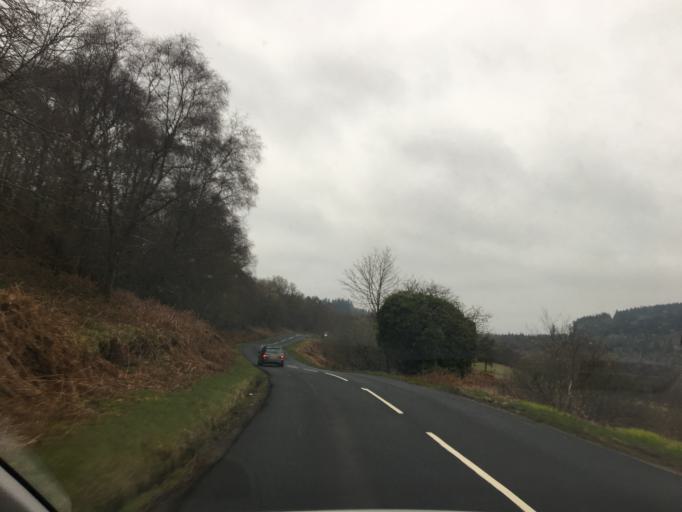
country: GB
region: Scotland
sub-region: North Ayrshire
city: Lamlash
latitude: 55.5468
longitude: -5.1351
